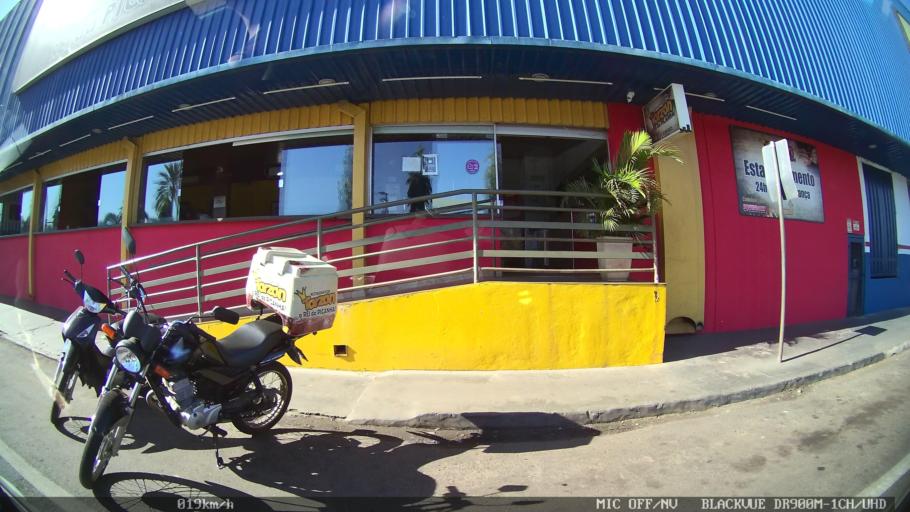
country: BR
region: Sao Paulo
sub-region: Olimpia
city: Olimpia
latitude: -20.7303
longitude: -48.9132
